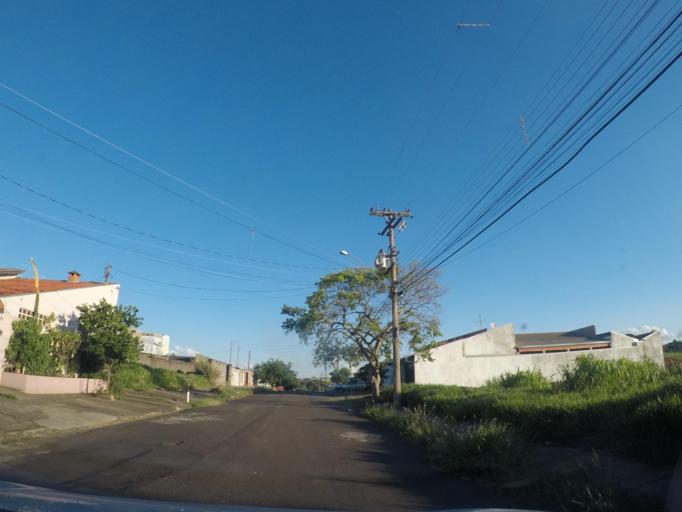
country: BR
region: Sao Paulo
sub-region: Sumare
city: Sumare
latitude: -22.8221
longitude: -47.2533
